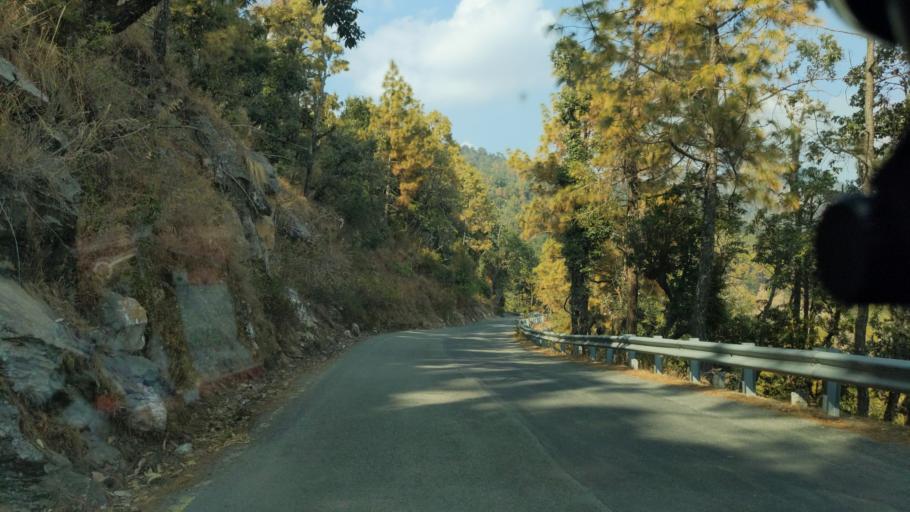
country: IN
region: Uttarakhand
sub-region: Naini Tal
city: Bhowali
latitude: 29.3985
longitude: 79.5353
